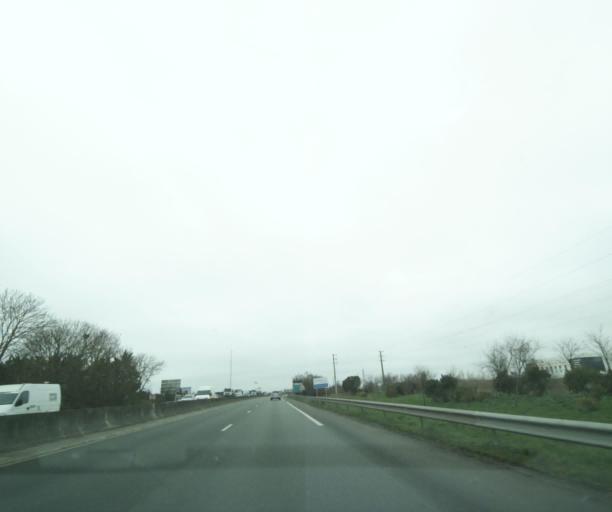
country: FR
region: Poitou-Charentes
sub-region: Departement de la Charente-Maritime
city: Perigny
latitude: 46.1578
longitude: -1.1185
